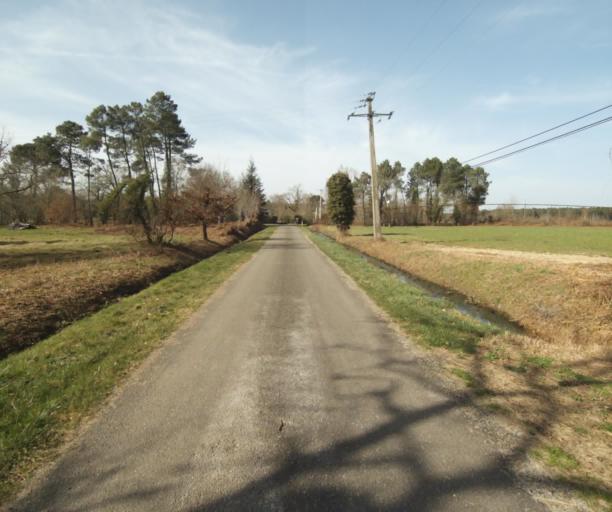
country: FR
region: Aquitaine
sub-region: Departement des Landes
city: Roquefort
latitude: 44.1596
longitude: -0.2024
